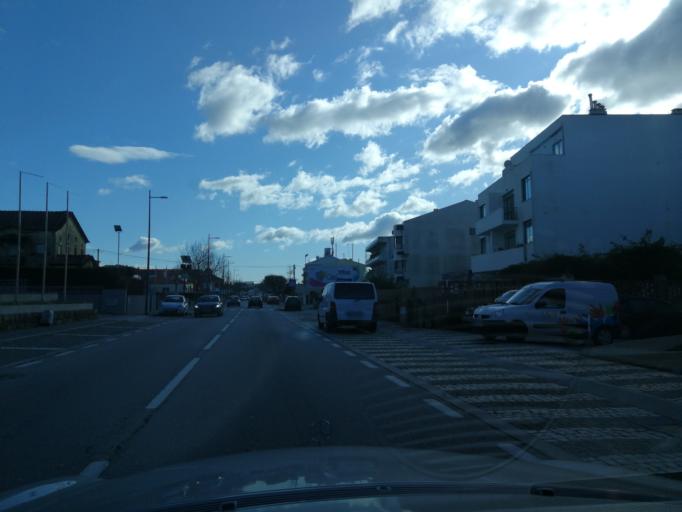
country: PT
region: Viana do Castelo
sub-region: Viana do Castelo
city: Viana do Castelo
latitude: 41.6974
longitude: -8.8443
